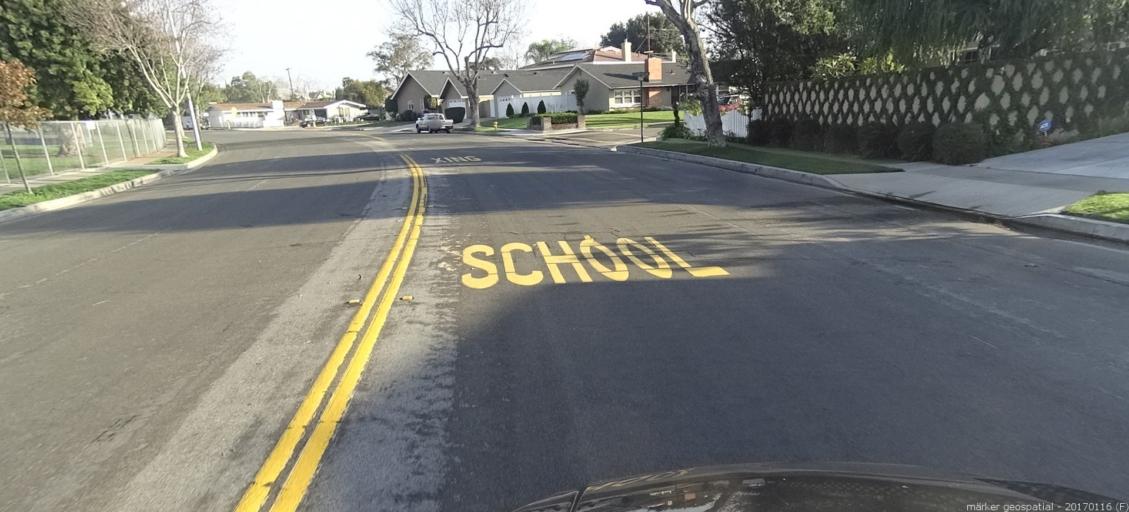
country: US
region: California
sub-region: Orange County
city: Rossmoor
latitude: 33.7915
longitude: -118.0765
